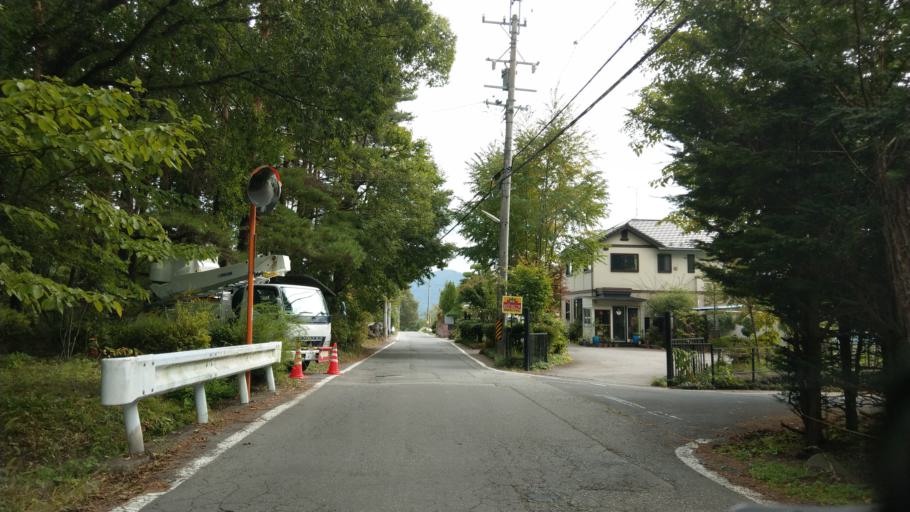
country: JP
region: Nagano
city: Komoro
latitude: 36.3253
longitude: 138.5270
